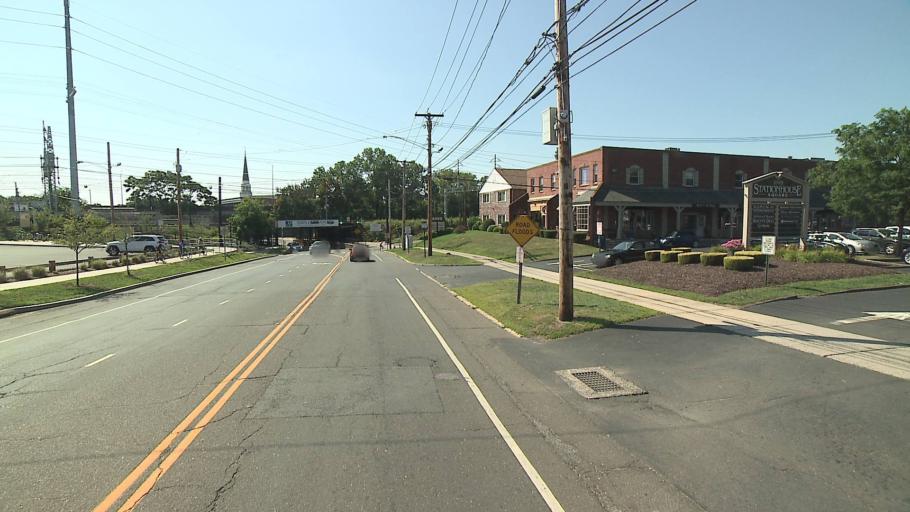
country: US
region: Connecticut
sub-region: Fairfield County
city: Stratford
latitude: 41.1949
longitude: -73.1319
